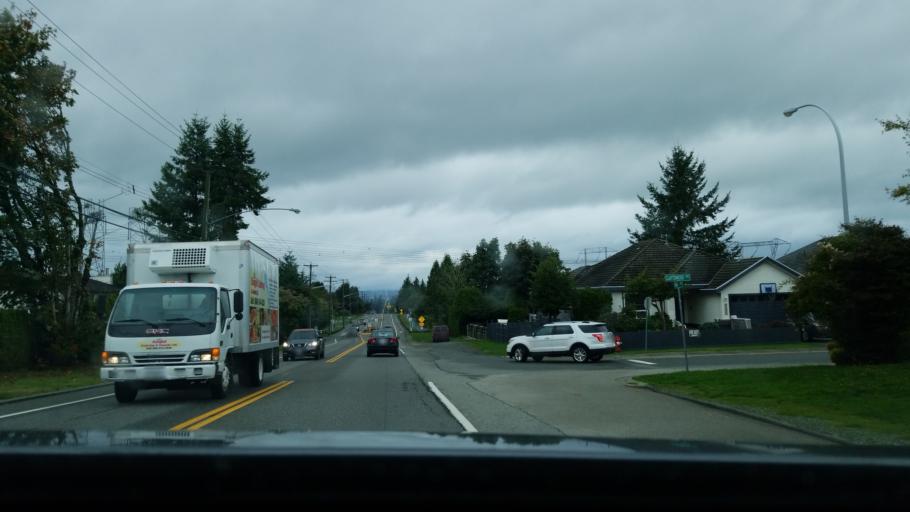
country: CA
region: British Columbia
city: Langley
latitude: 49.1188
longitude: -122.7165
